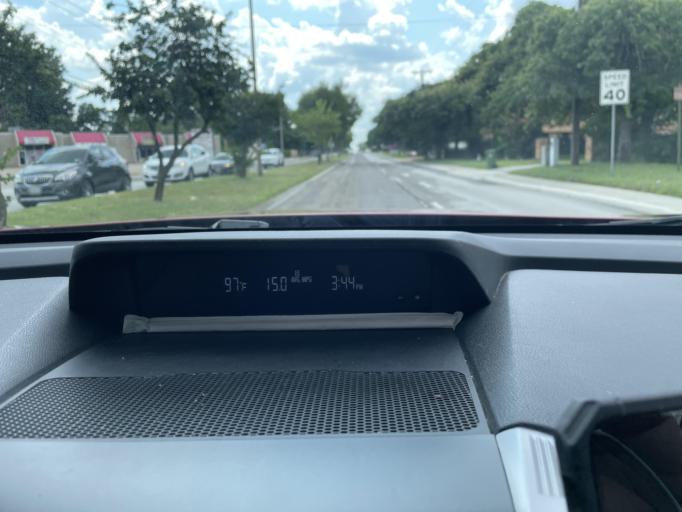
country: US
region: Texas
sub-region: Tarrant County
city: Dalworthington Gardens
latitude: 32.7067
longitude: -97.1283
